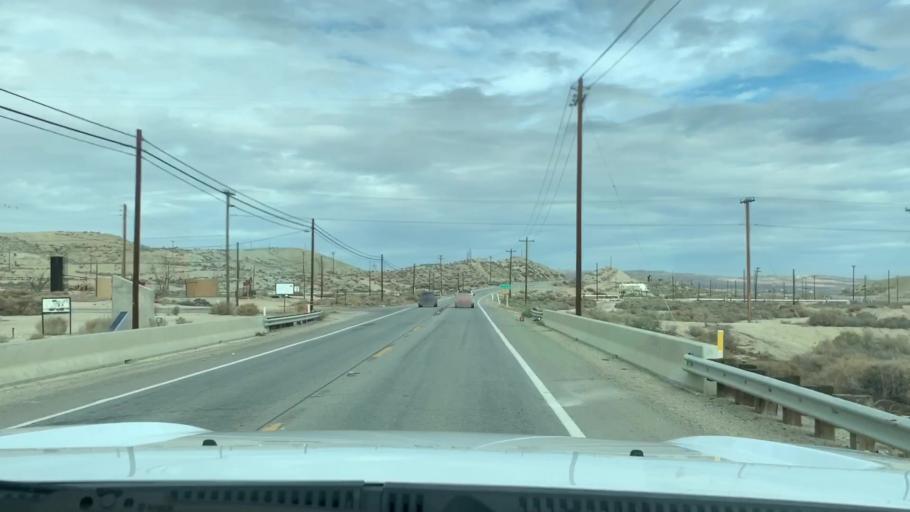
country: US
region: California
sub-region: Kern County
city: Maricopa
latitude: 35.0742
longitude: -119.4019
